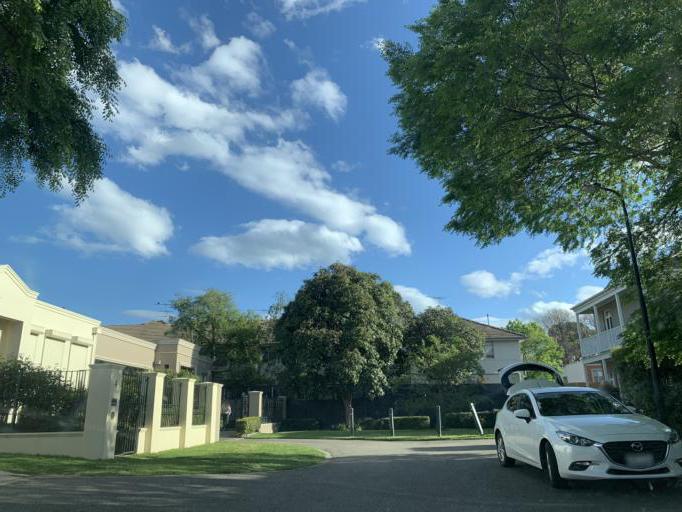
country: AU
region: Victoria
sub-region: Bayside
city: North Brighton
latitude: -37.9032
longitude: 144.9973
